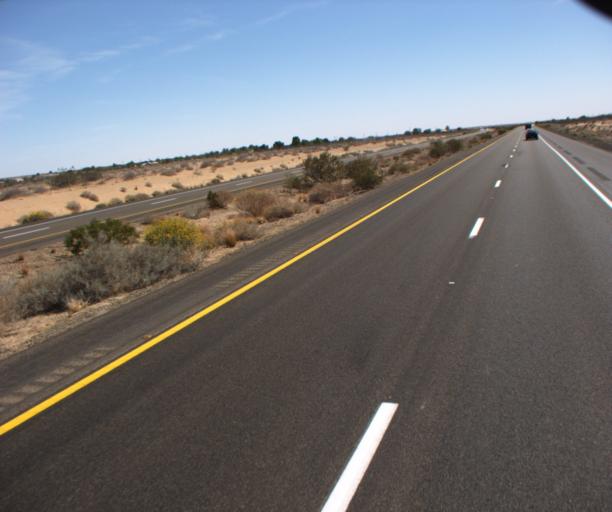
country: US
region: Arizona
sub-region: Yuma County
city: Fortuna Foothills
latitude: 32.6410
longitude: -114.5215
